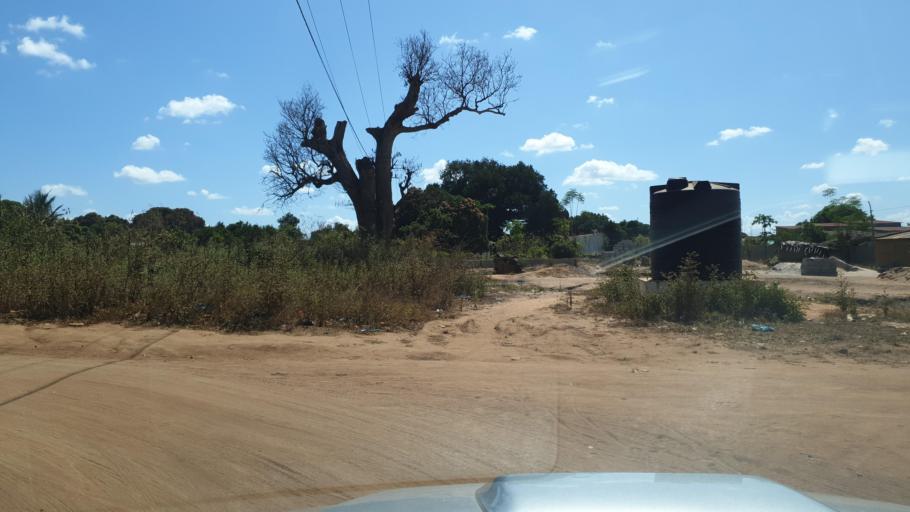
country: MZ
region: Nampula
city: Nampula
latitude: -15.1092
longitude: 39.2066
